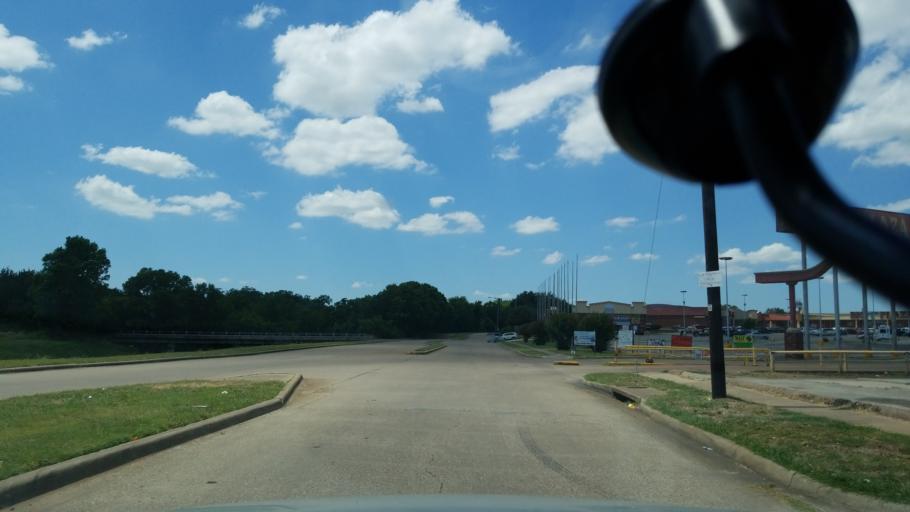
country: US
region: Texas
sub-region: Dallas County
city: Cockrell Hill
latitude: 32.6899
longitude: -96.8285
